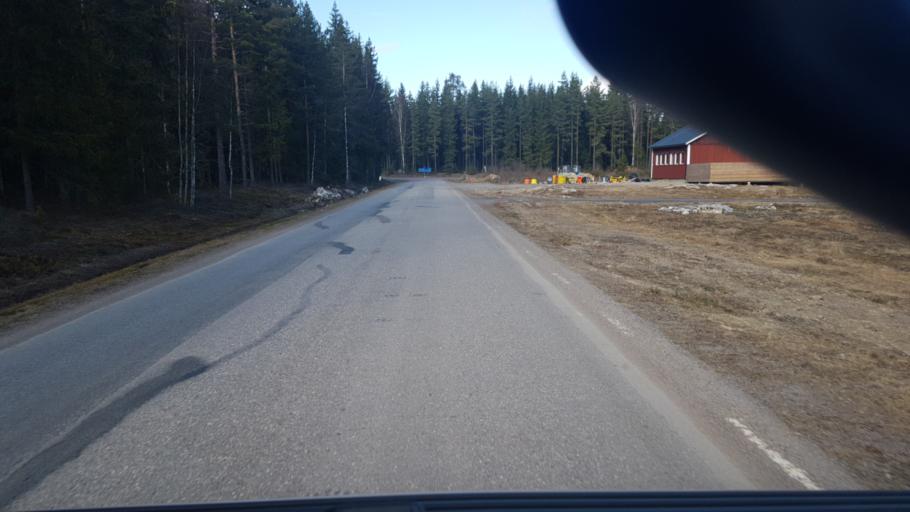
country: SE
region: Vaermland
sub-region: Eda Kommun
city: Charlottenberg
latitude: 59.8841
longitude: 12.3560
